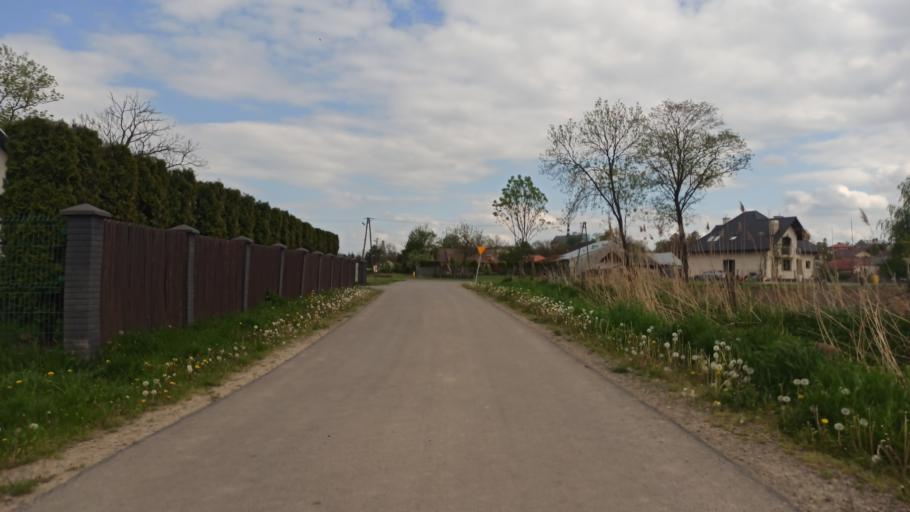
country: PL
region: Subcarpathian Voivodeship
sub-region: Powiat jaroslawski
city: Radymno
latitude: 49.9577
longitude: 22.8130
